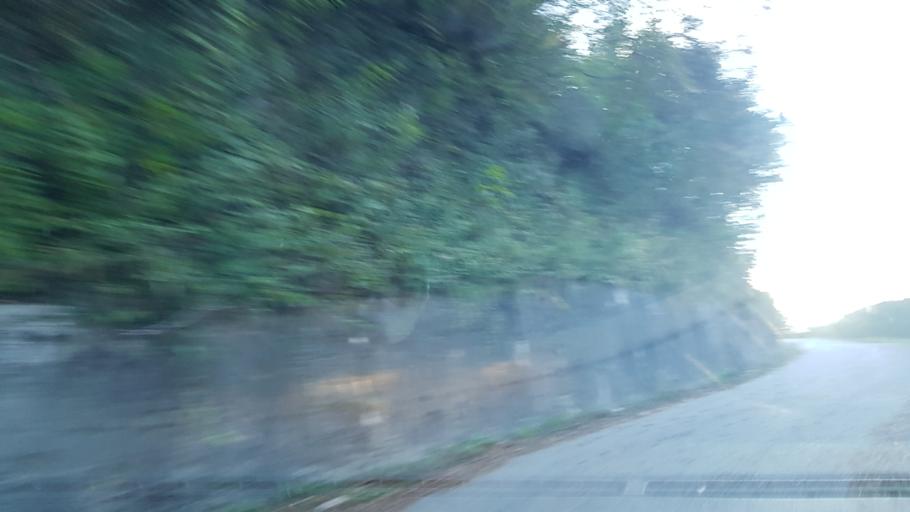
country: IT
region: Friuli Venezia Giulia
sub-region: Provincia di Udine
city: Venzone
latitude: 46.3348
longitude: 13.1581
